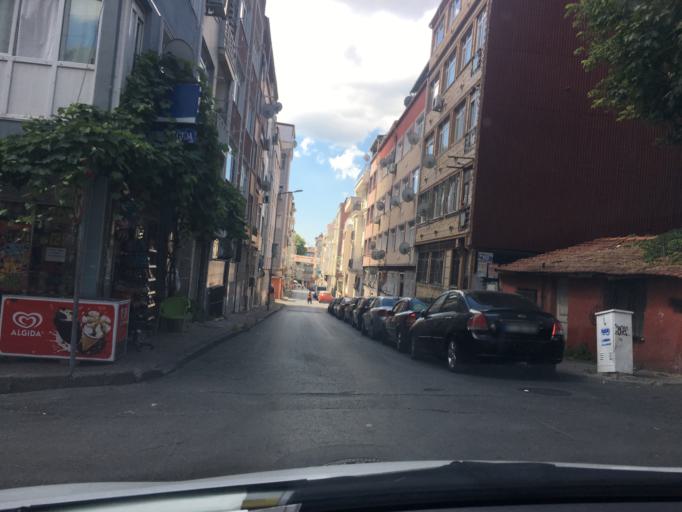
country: TR
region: Istanbul
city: Istanbul
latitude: 41.0090
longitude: 28.9334
